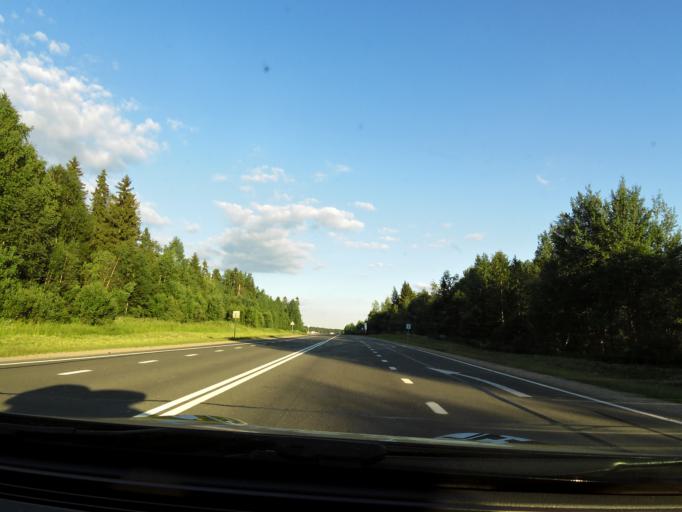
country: RU
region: Vologda
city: Vologda
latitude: 59.0793
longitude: 40.0155
